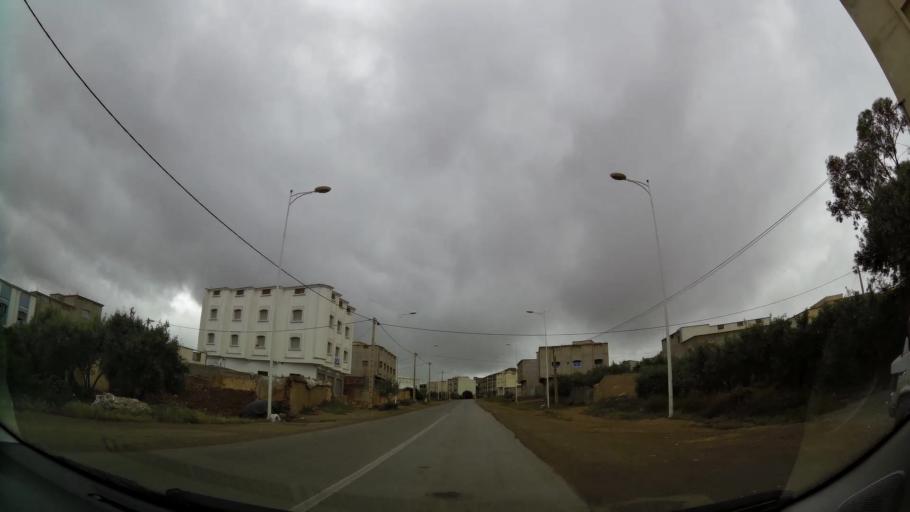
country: MA
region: Oriental
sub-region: Nador
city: Midar
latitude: 35.0559
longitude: -3.4633
